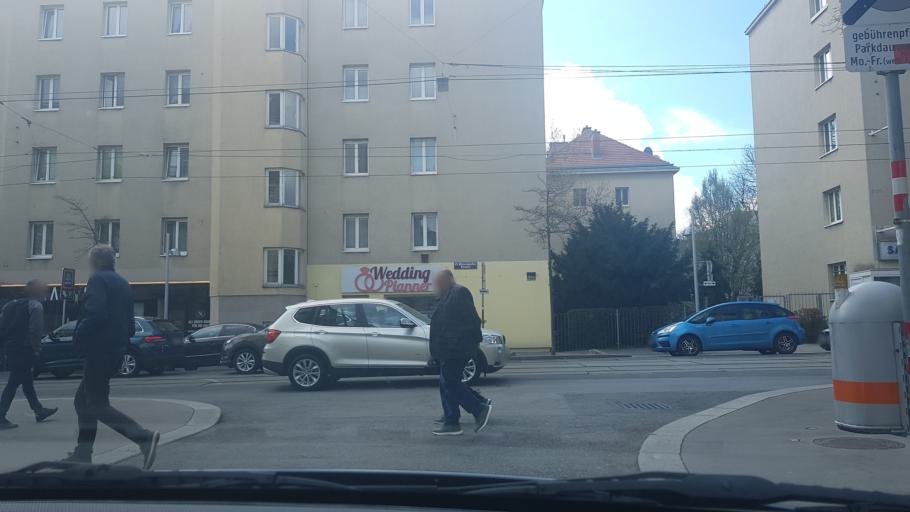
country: AT
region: Vienna
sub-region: Wien Stadt
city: Vienna
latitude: 48.1992
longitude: 16.3225
